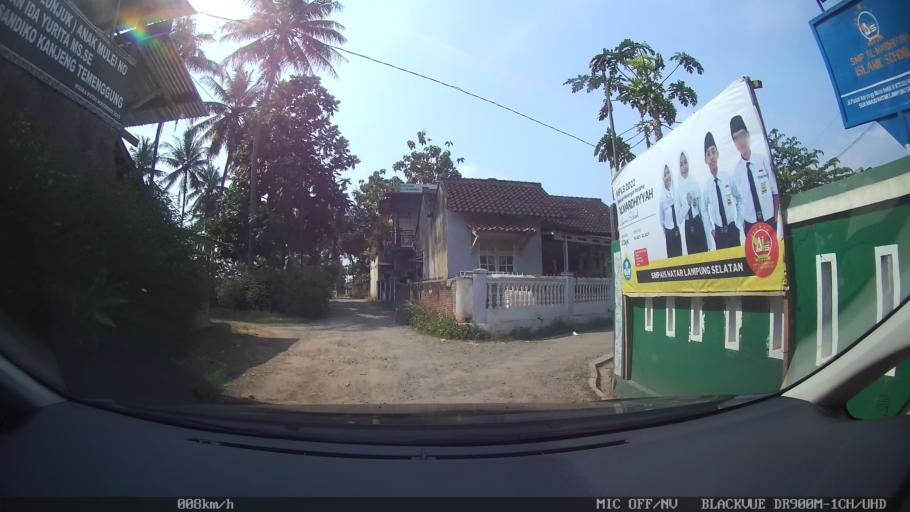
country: ID
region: Lampung
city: Natar
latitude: -5.3141
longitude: 105.2039
